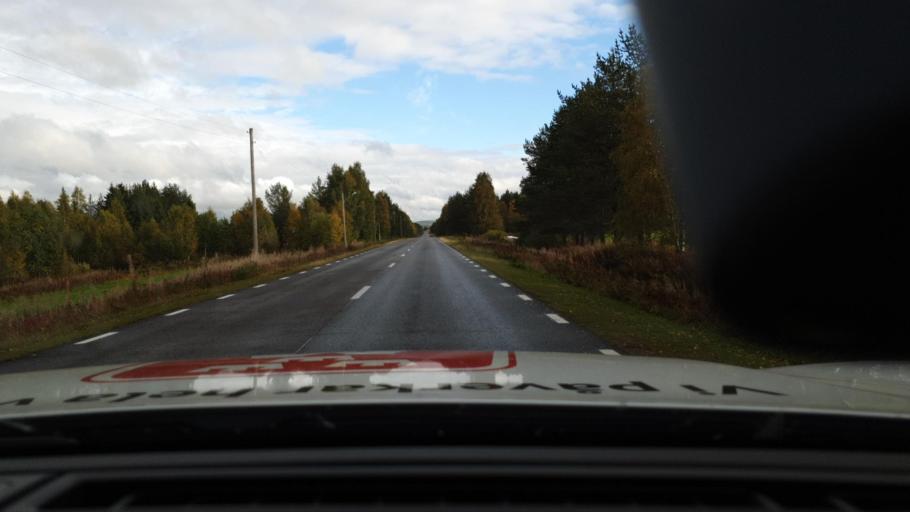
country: SE
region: Norrbotten
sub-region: Overkalix Kommun
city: OEverkalix
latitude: 66.9514
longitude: 22.7078
